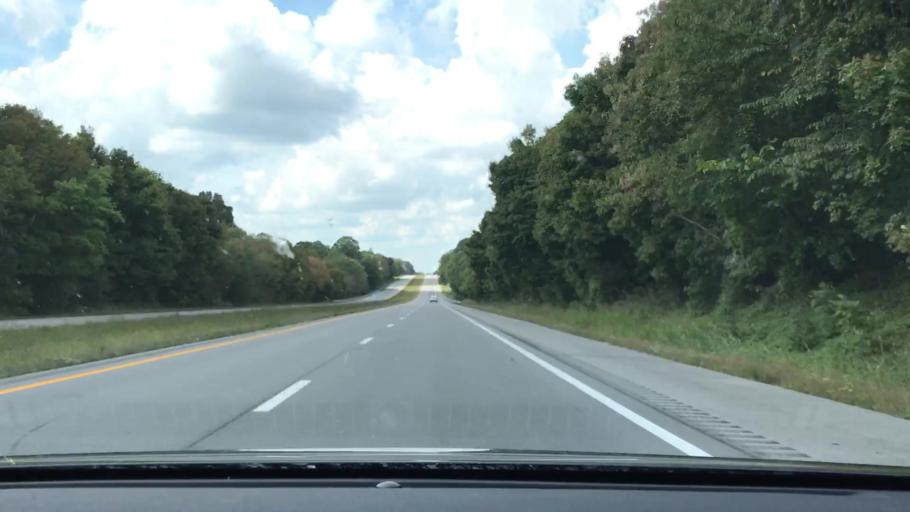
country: US
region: Kentucky
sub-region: Adair County
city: Columbia
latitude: 37.0719
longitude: -85.2177
